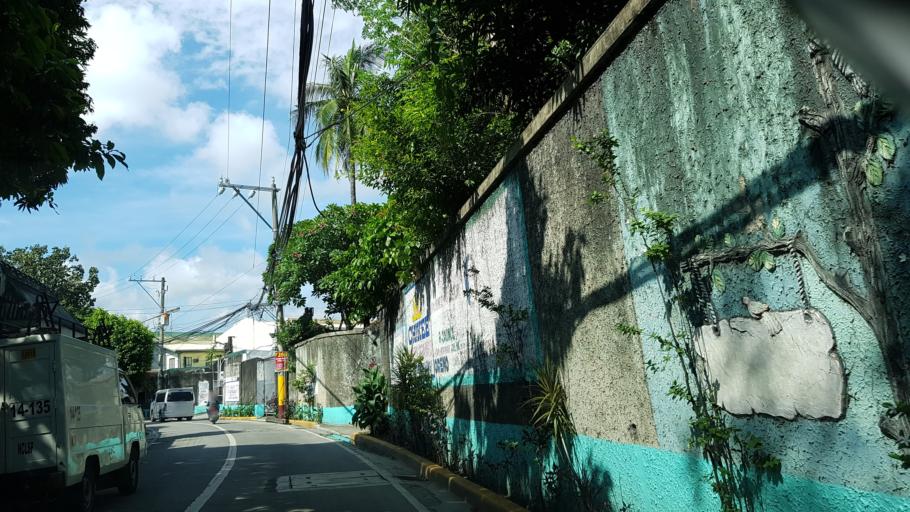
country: PH
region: Metro Manila
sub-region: San Juan
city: San Juan
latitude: 14.5834
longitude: 121.0181
